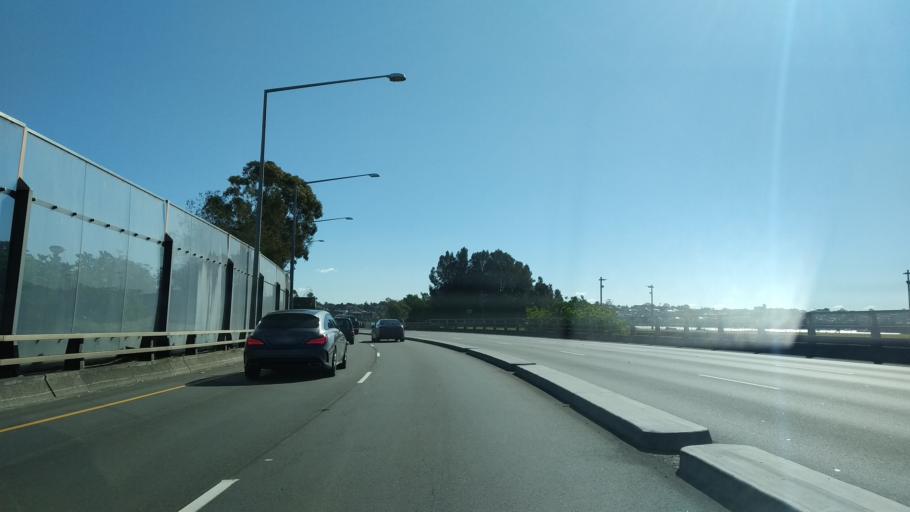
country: AU
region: New South Wales
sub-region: Leichhardt
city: Leichhardt
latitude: -33.8728
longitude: 151.1501
